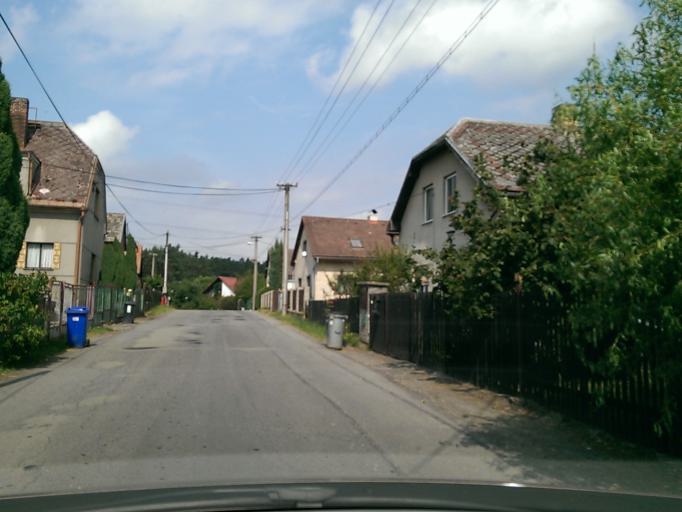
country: CZ
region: Central Bohemia
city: Bakov nad Jizerou
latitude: 50.4756
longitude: 14.8865
